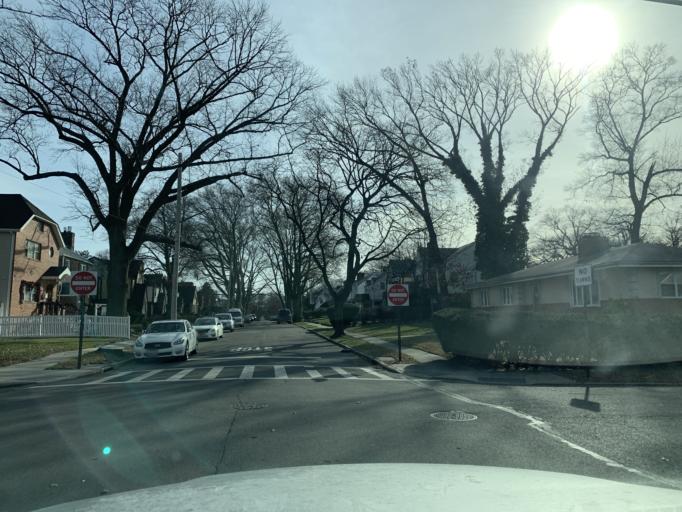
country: US
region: New York
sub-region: Queens County
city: Jamaica
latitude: 40.6972
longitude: -73.7726
